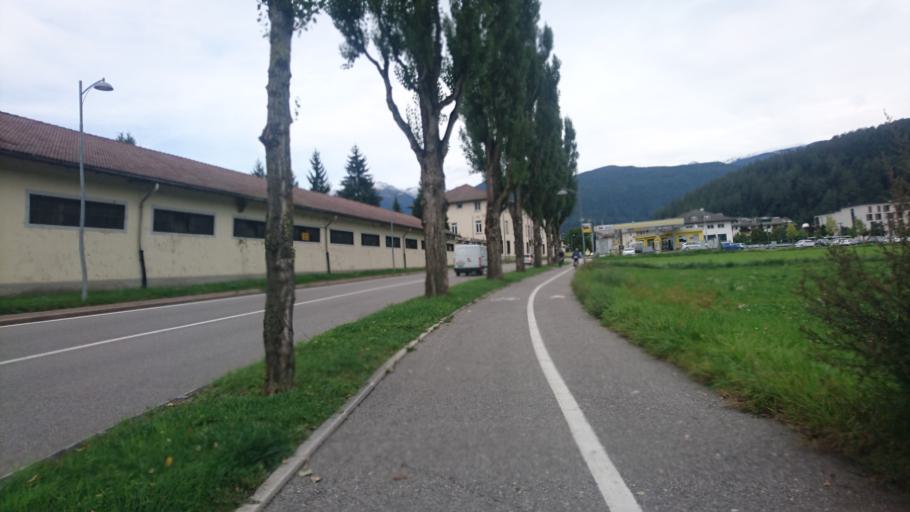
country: IT
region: Trentino-Alto Adige
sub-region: Bolzano
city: Brunico
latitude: 46.7901
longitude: 11.9257
